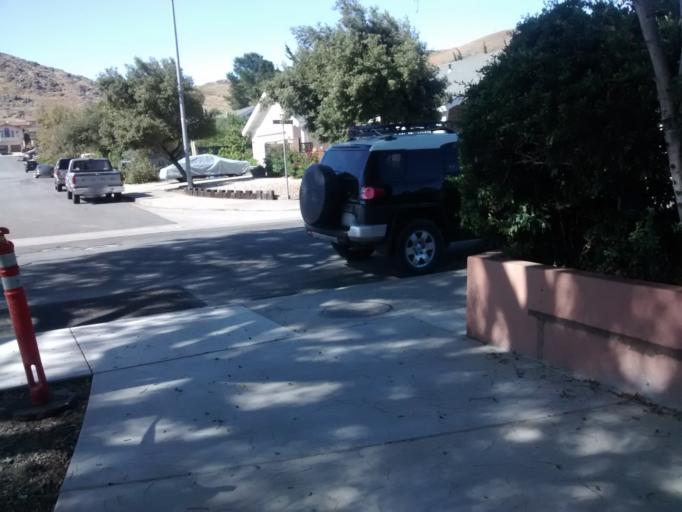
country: US
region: California
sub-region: San Luis Obispo County
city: San Luis Obispo
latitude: 35.2671
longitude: -120.6621
